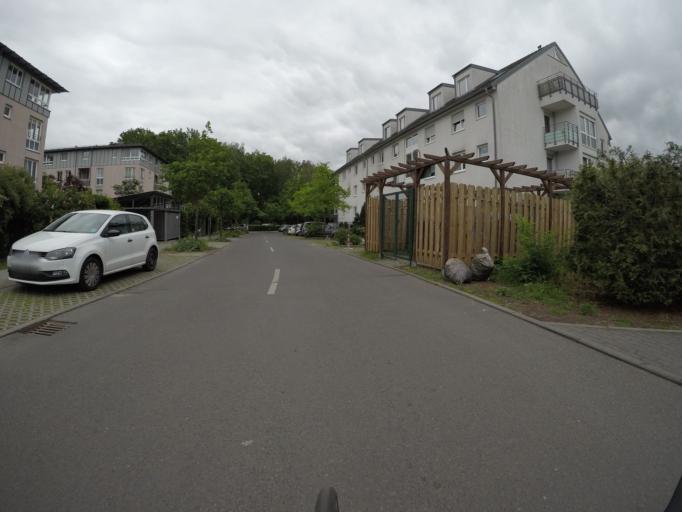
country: DE
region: Brandenburg
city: Glienicke
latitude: 52.6447
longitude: 13.3172
